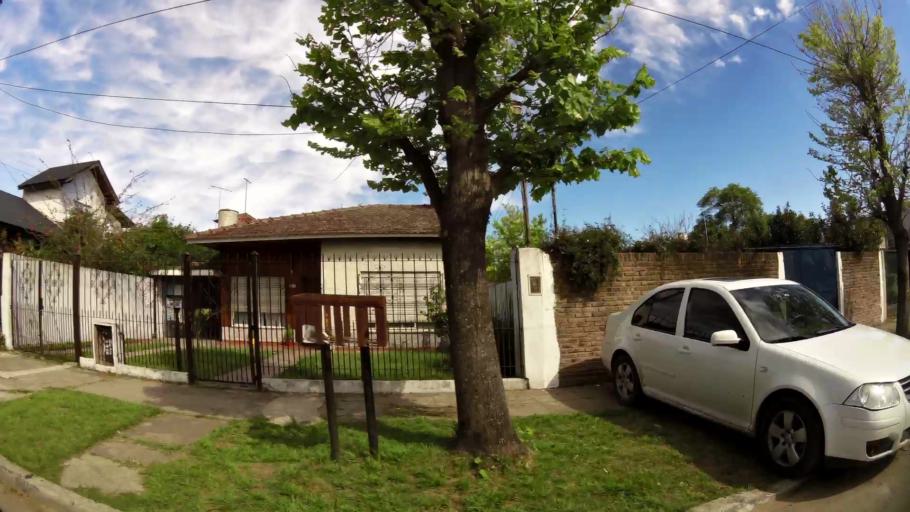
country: AR
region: Buenos Aires
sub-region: Partido de Quilmes
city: Quilmes
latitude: -34.7829
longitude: -58.3025
